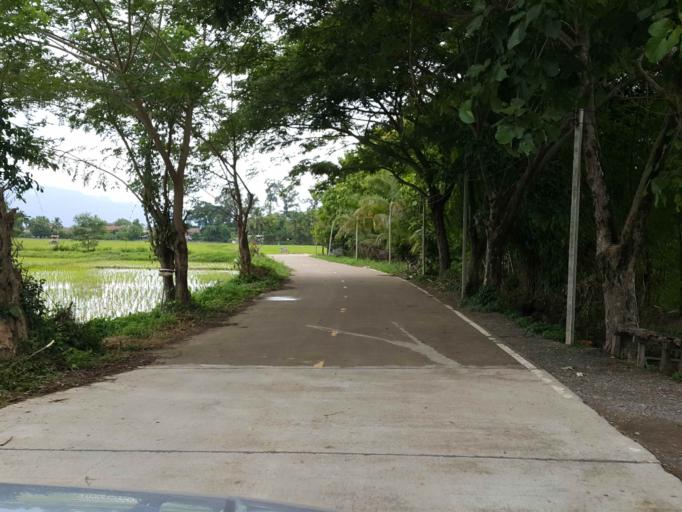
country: TH
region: Chiang Mai
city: San Sai
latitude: 18.8227
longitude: 99.0687
